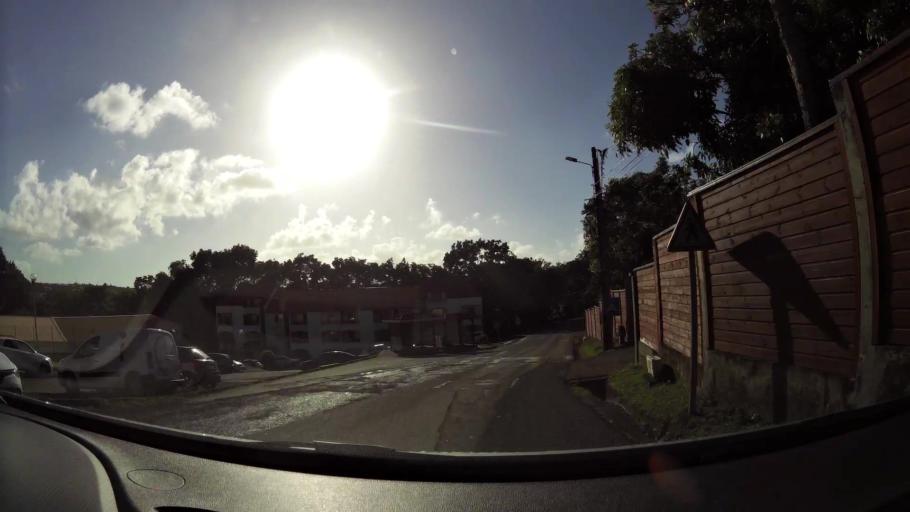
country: MQ
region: Martinique
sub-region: Martinique
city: Le Lamentin
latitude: 14.6266
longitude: -61.0256
